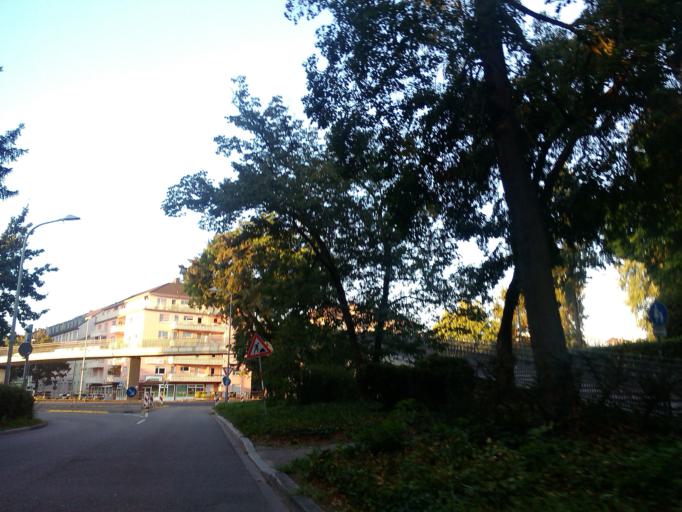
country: DE
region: Baden-Wuerttemberg
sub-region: Karlsruhe Region
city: Karlsruhe
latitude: 49.0061
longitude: 8.3985
